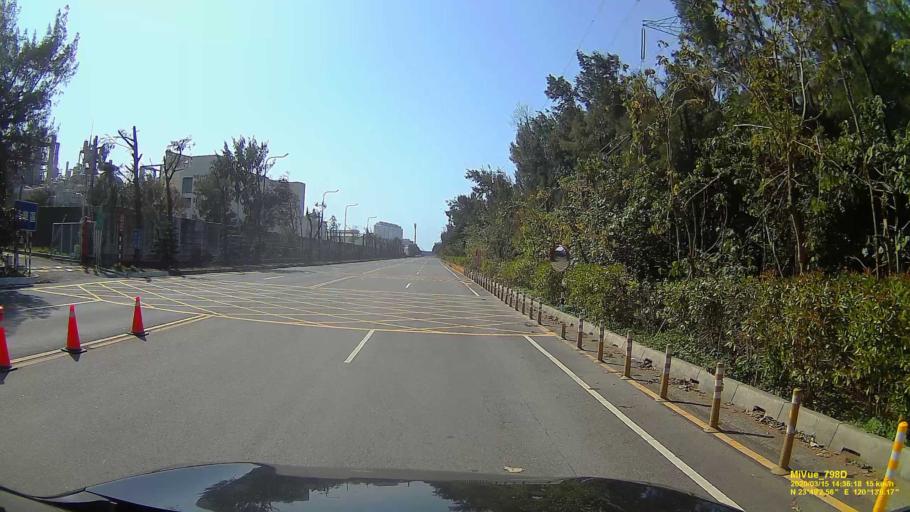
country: TW
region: Taiwan
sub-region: Yunlin
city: Douliu
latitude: 23.8174
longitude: 120.2182
